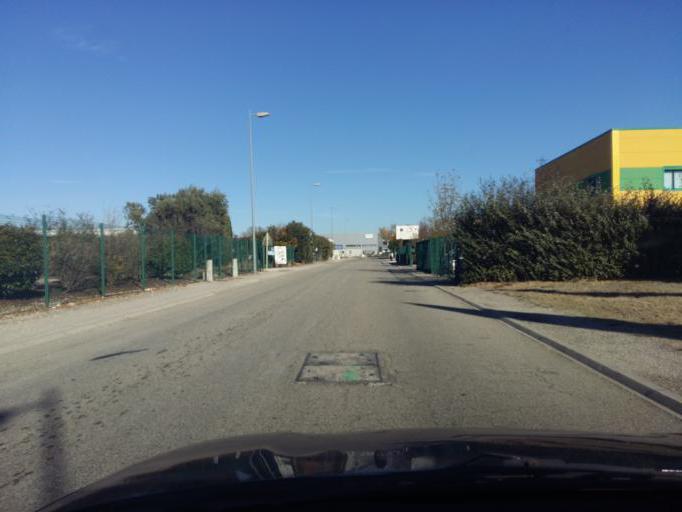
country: FR
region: Provence-Alpes-Cote d'Azur
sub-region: Departement du Vaucluse
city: Monteux
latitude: 44.0340
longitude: 4.9706
